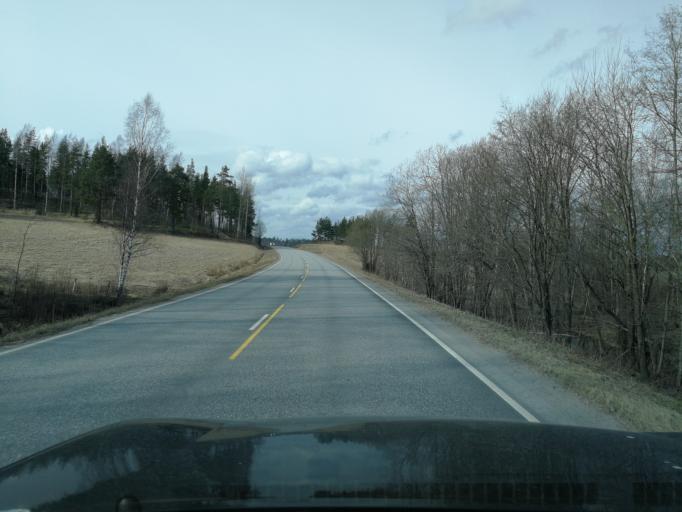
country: FI
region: Uusimaa
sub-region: Helsinki
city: Siuntio
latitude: 60.1073
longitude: 24.2460
